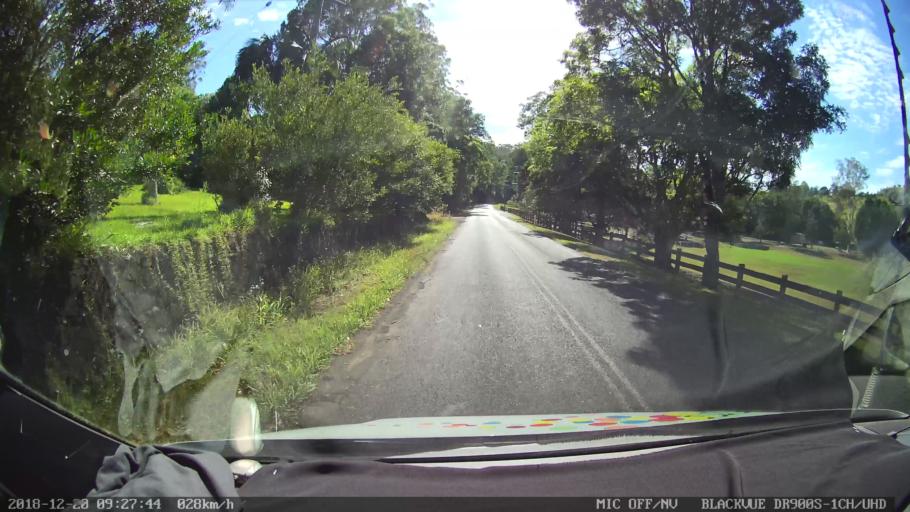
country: AU
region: New South Wales
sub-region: Lismore Municipality
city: Nimbin
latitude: -28.6789
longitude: 153.2804
